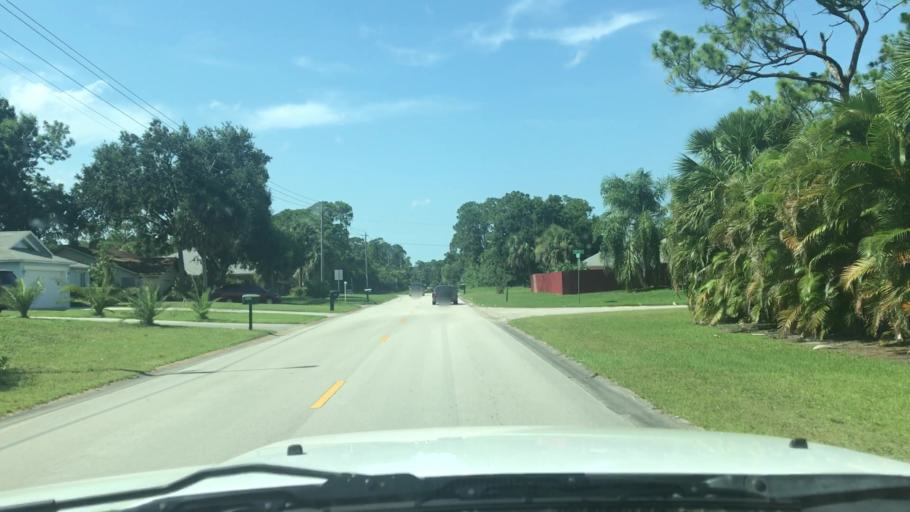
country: US
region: Florida
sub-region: Indian River County
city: Florida Ridge
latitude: 27.5673
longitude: -80.3980
